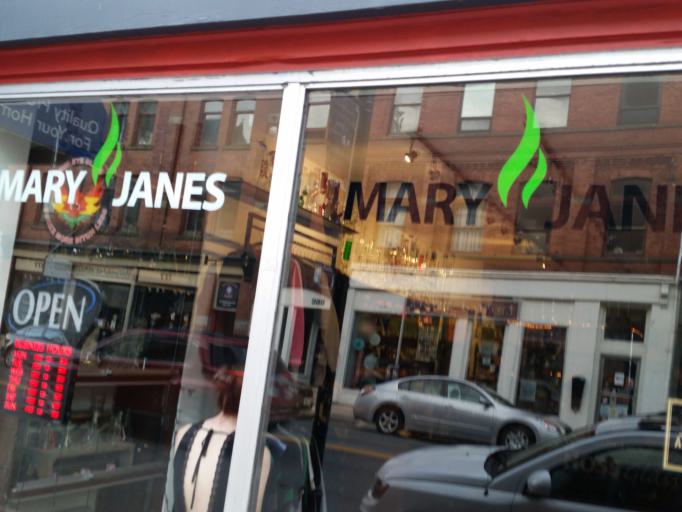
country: CA
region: Newfoundland and Labrador
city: St. John's
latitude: 47.5650
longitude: -52.7063
